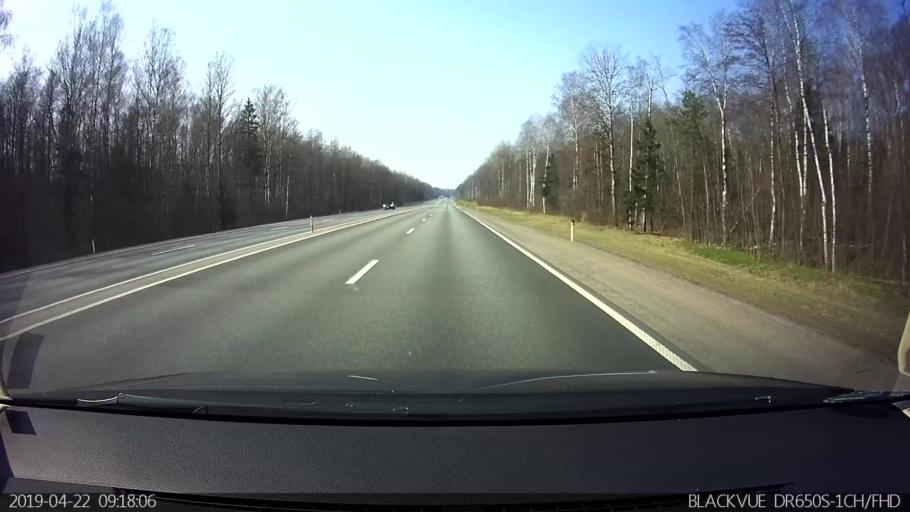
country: RU
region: Smolensk
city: Golynki
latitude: 54.7569
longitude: 31.4998
